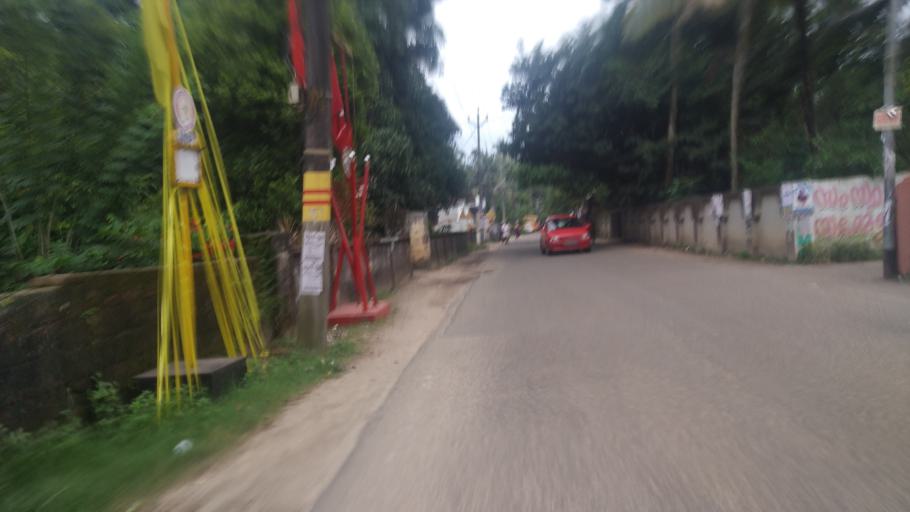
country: IN
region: Kerala
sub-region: Alappuzha
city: Arukutti
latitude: 9.8715
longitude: 76.2903
